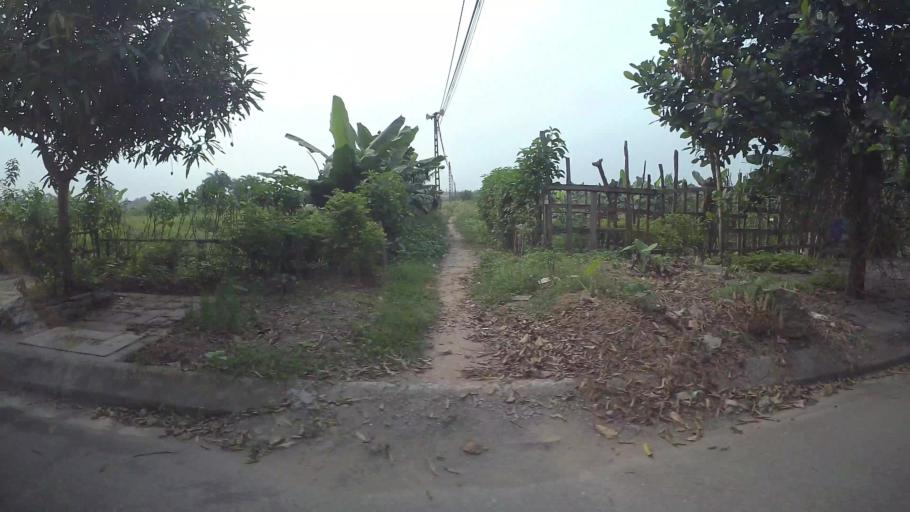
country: VN
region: Ha Noi
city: Hoan Kiem
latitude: 21.0702
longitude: 105.8961
